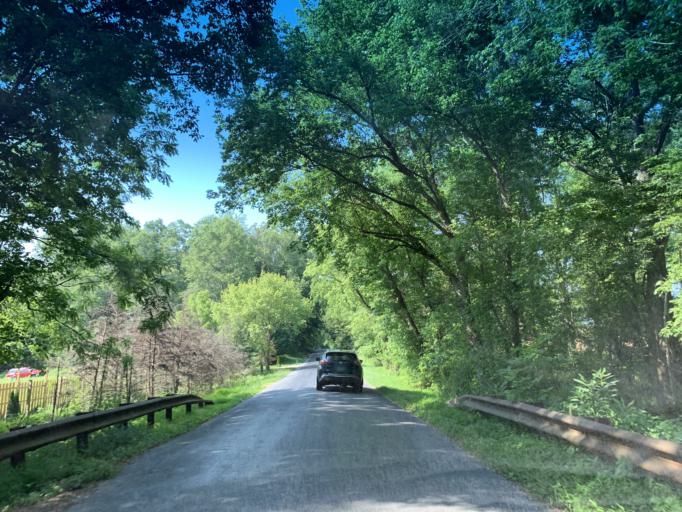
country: US
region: Maryland
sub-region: Montgomery County
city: Poolesville
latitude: 39.1270
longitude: -77.4527
